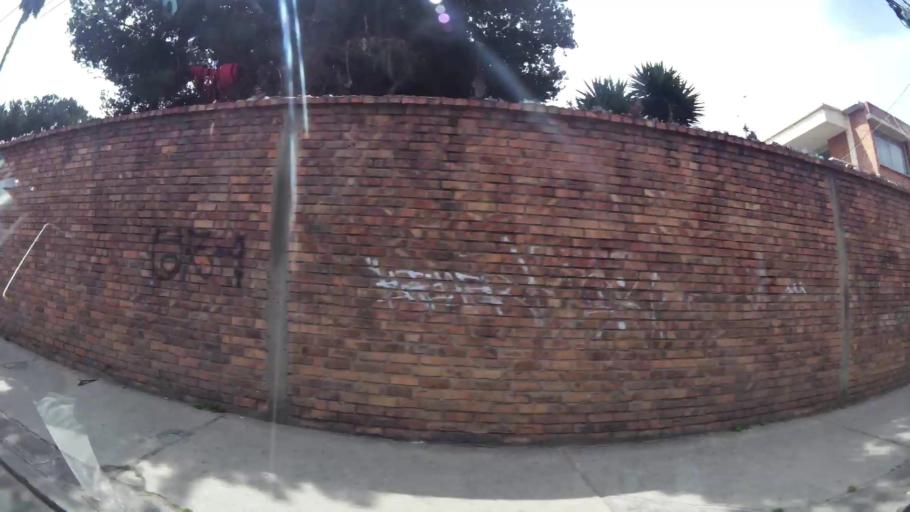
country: CO
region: Bogota D.C.
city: Bogota
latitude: 4.5701
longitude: -74.0978
